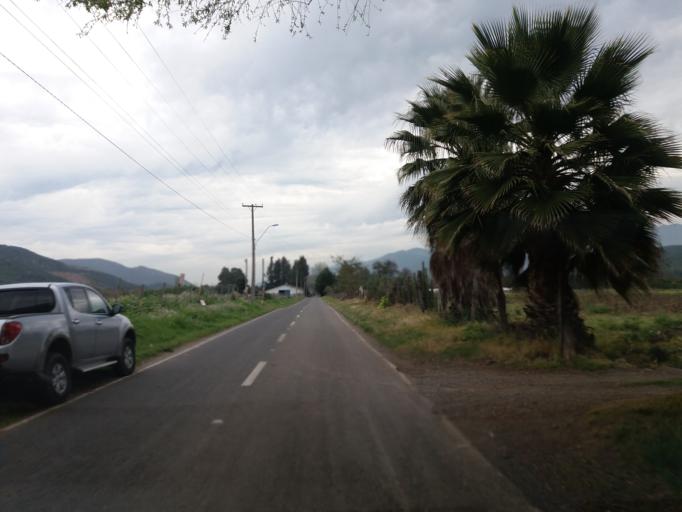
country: CL
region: Valparaiso
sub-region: Provincia de Quillota
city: Quillota
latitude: -32.8897
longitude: -71.1080
